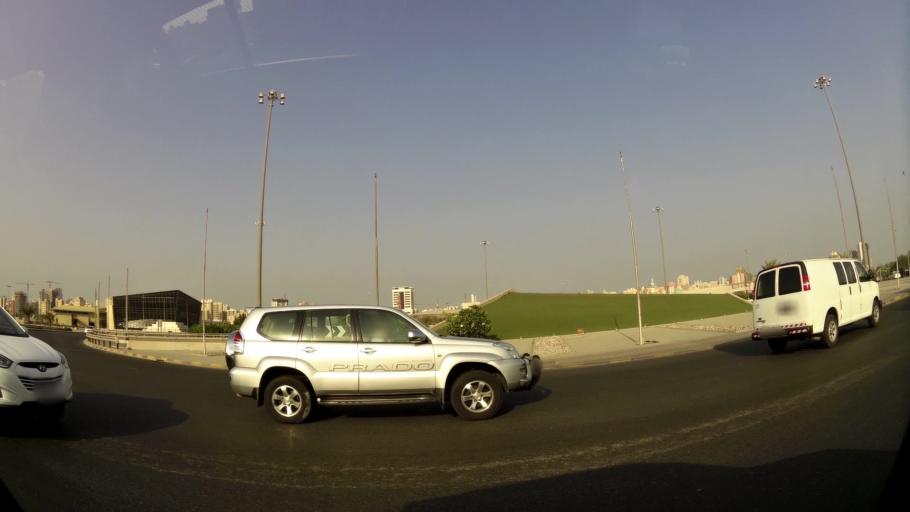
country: KW
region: Muhafazat Hawalli
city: As Salimiyah
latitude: 29.3254
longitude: 48.0772
